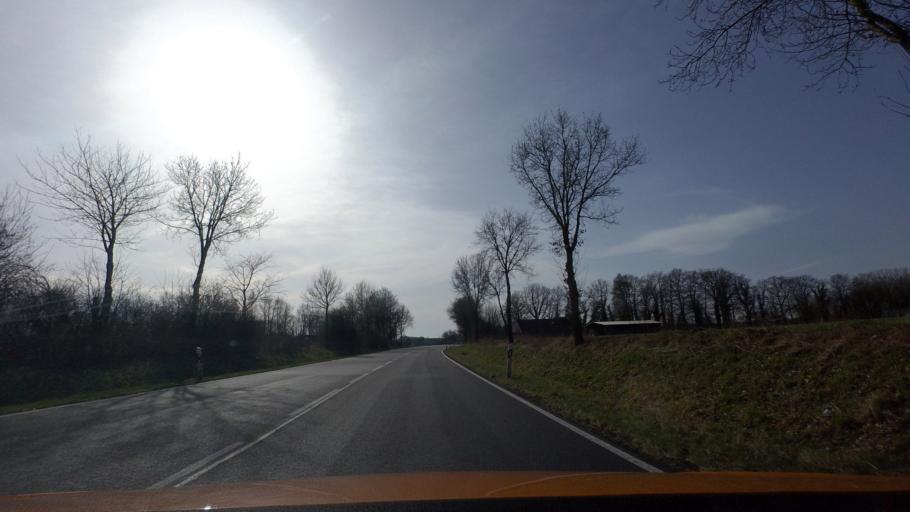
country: DE
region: North Rhine-Westphalia
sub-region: Regierungsbezirk Detmold
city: Petershagen
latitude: 52.3928
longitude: 8.9572
